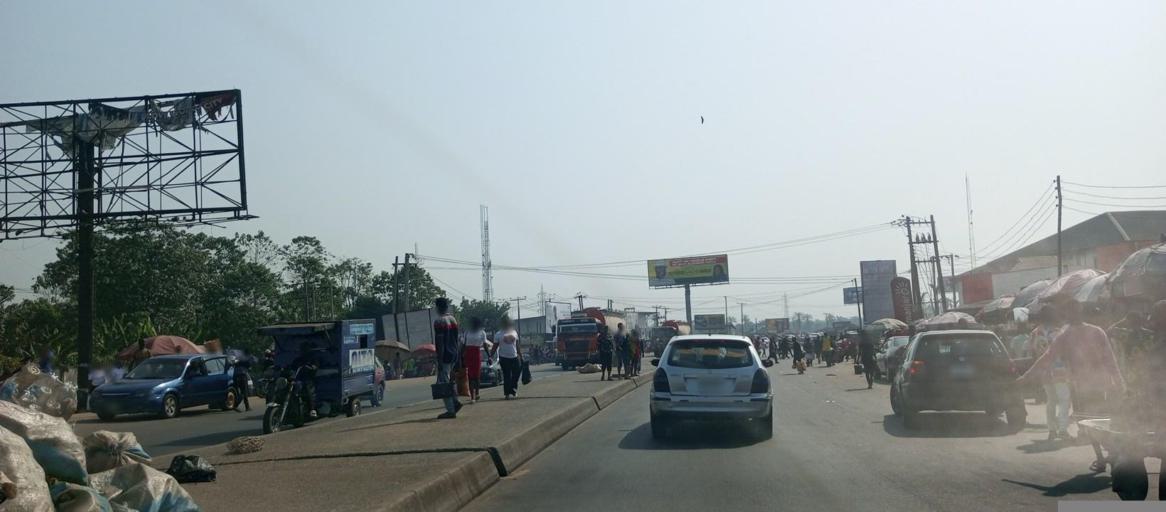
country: NG
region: Rivers
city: Emuoha
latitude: 4.8989
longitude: 6.9060
